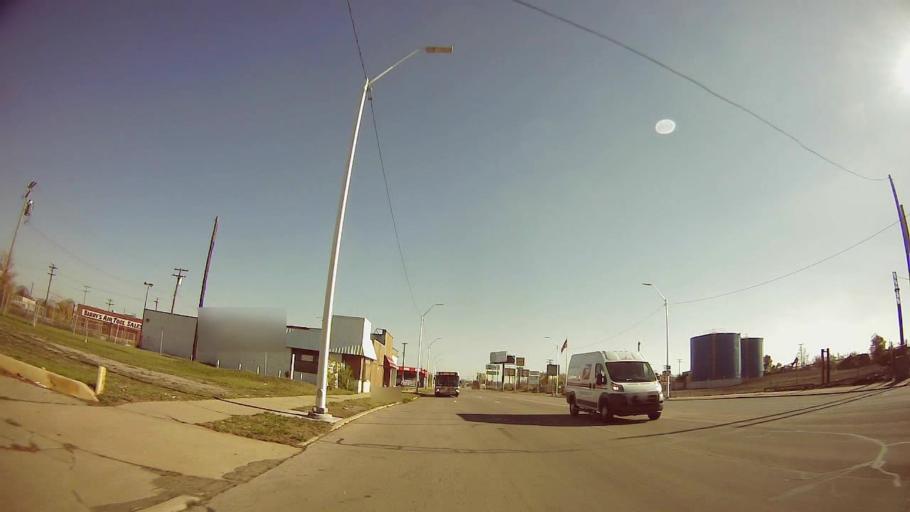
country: US
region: Michigan
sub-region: Wayne County
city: Dearborn
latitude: 42.3729
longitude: -83.1490
